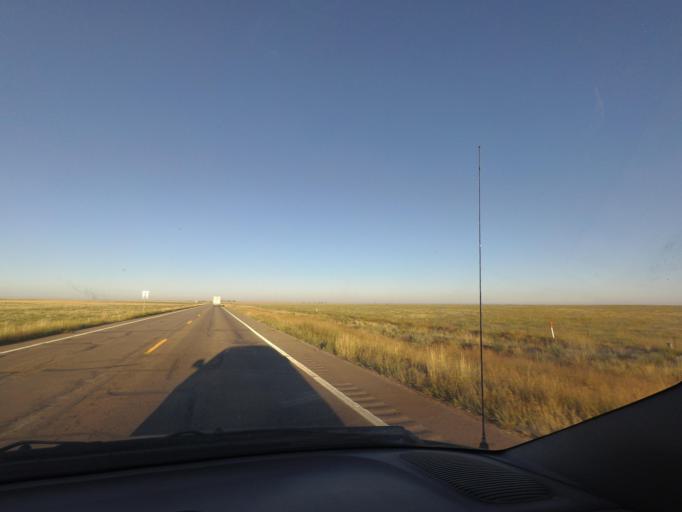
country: US
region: Colorado
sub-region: Yuma County
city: Yuma
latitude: 39.6711
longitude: -102.8636
